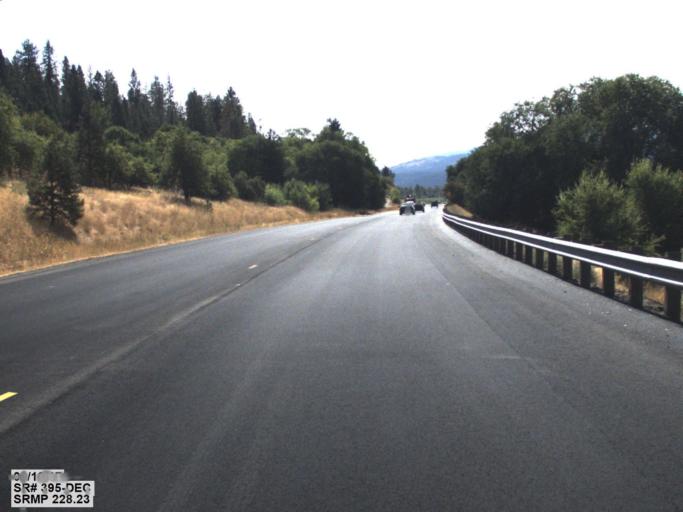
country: US
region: Washington
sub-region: Stevens County
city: Colville
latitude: 48.5264
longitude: -117.9027
